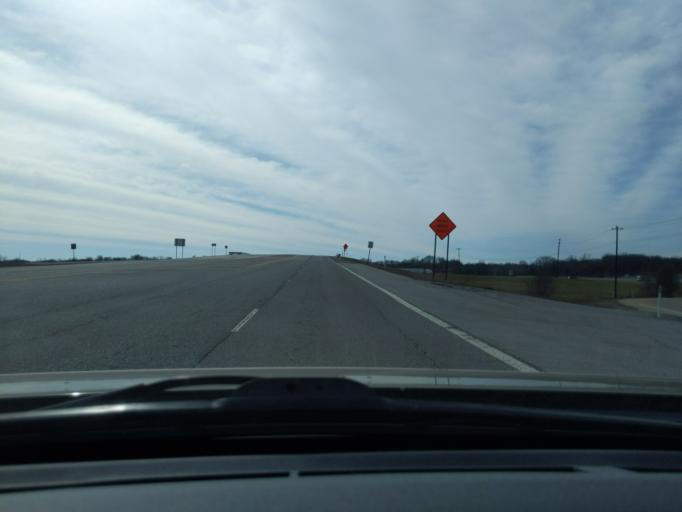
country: US
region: Tennessee
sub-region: Wilson County
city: Mount Juliet
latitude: 36.1804
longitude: -86.4570
